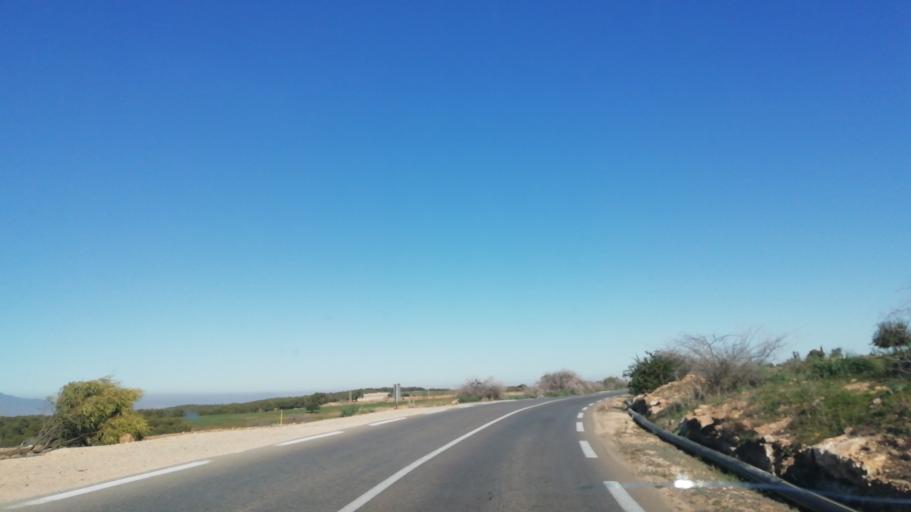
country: DZ
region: Tlemcen
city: Beni Mester
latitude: 34.8199
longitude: -1.6144
